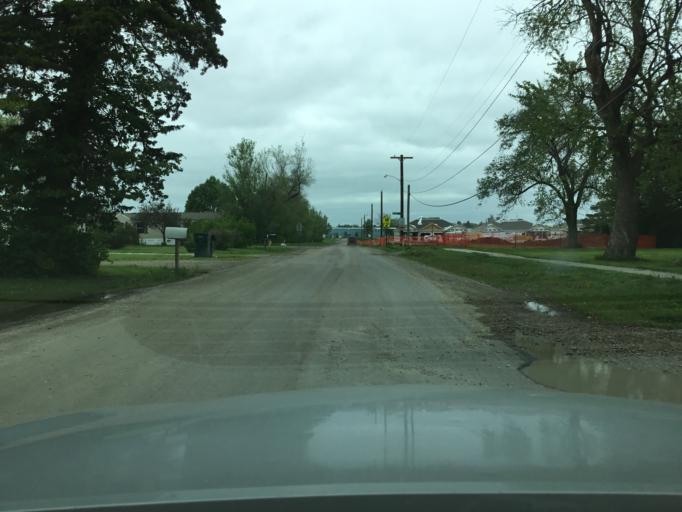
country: US
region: Kansas
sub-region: Franklin County
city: Ottawa
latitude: 38.6340
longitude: -95.2585
